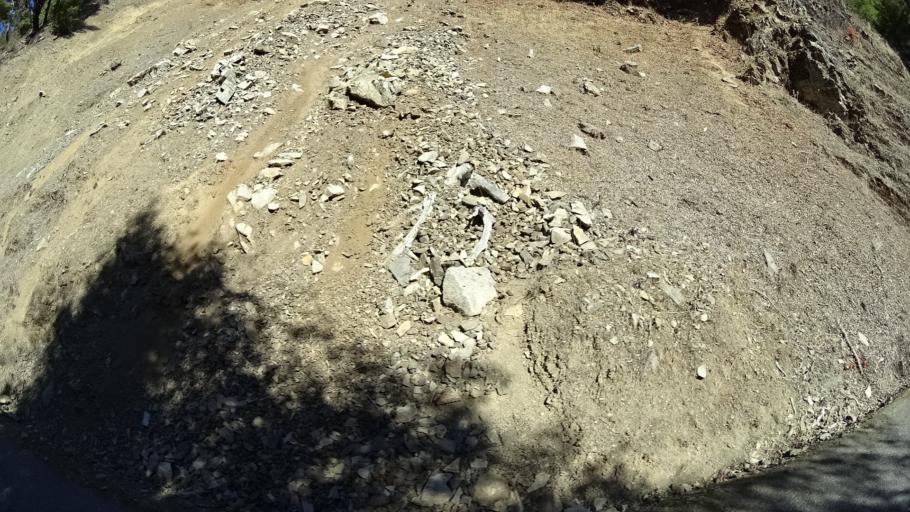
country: US
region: California
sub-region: Siskiyou County
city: Happy Camp
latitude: 41.3077
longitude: -123.1662
